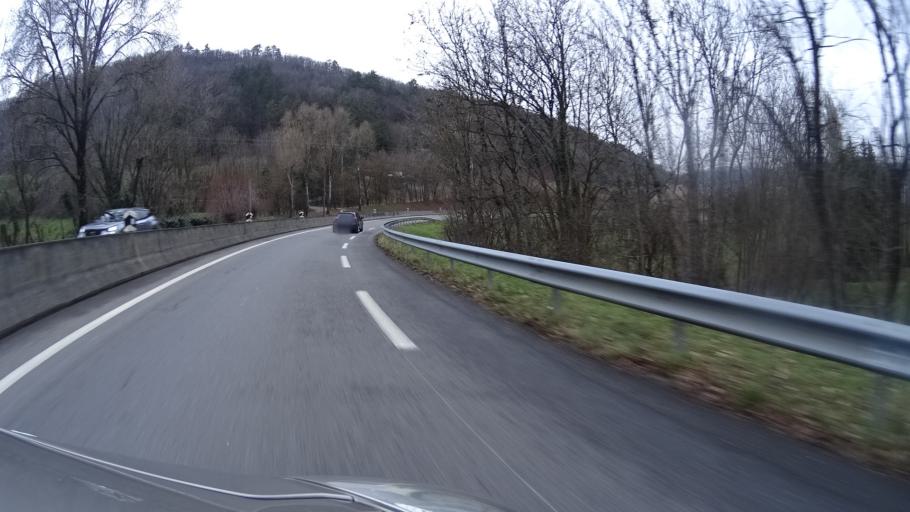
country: FR
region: Franche-Comte
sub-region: Departement du Doubs
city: Morre
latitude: 47.2208
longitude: 6.0611
